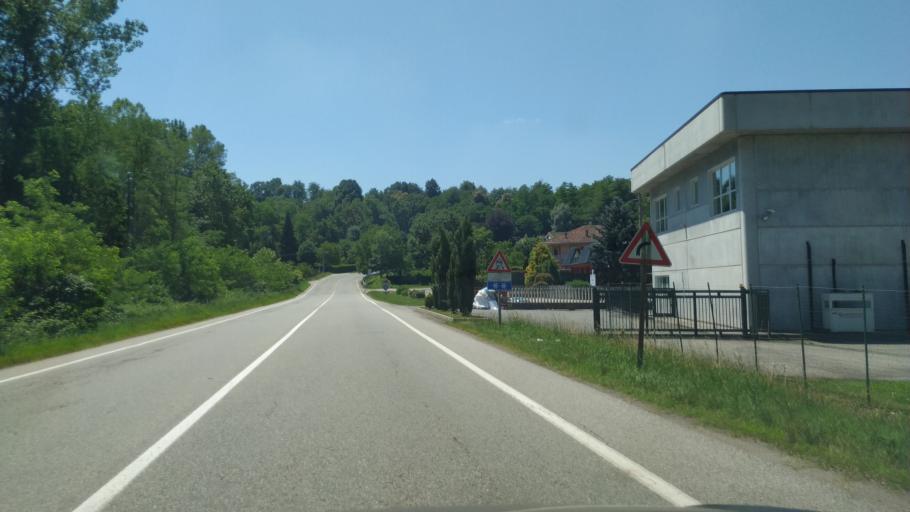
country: IT
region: Piedmont
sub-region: Provincia di Novara
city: Cureggio
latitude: 45.6698
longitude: 8.4536
